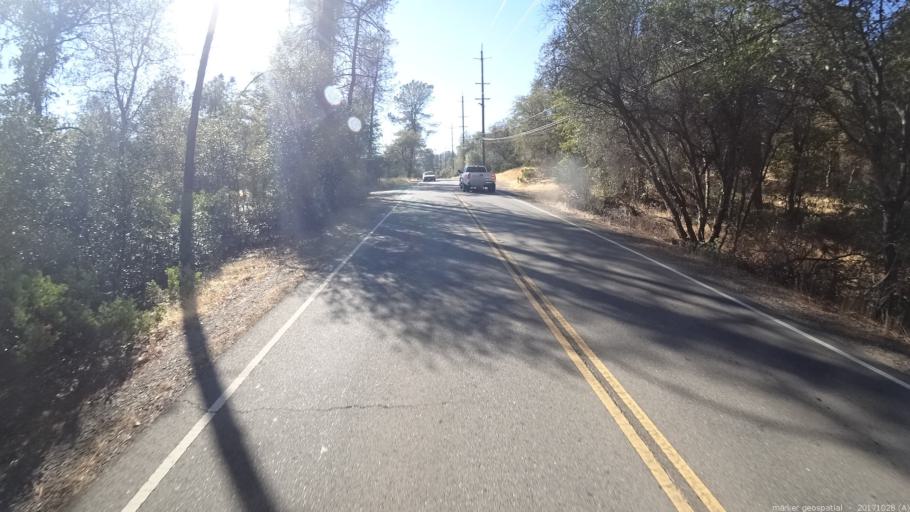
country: US
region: California
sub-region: Shasta County
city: Redding
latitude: 40.6245
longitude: -122.4180
